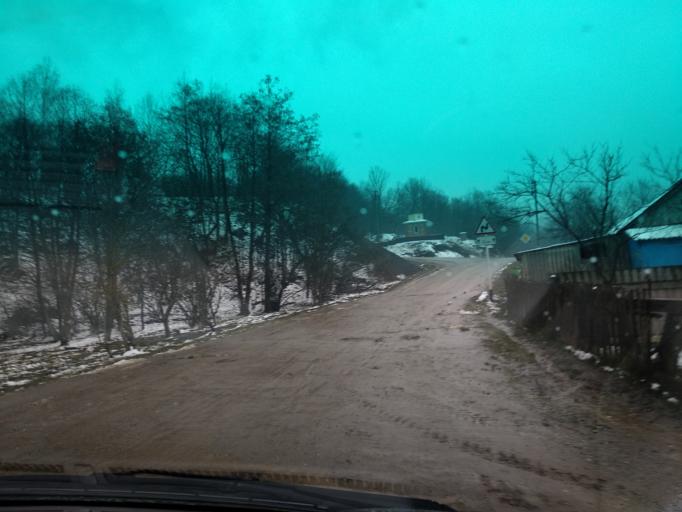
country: RU
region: Krasnodarskiy
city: Khadyzhensk
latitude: 44.2099
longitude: 39.4318
